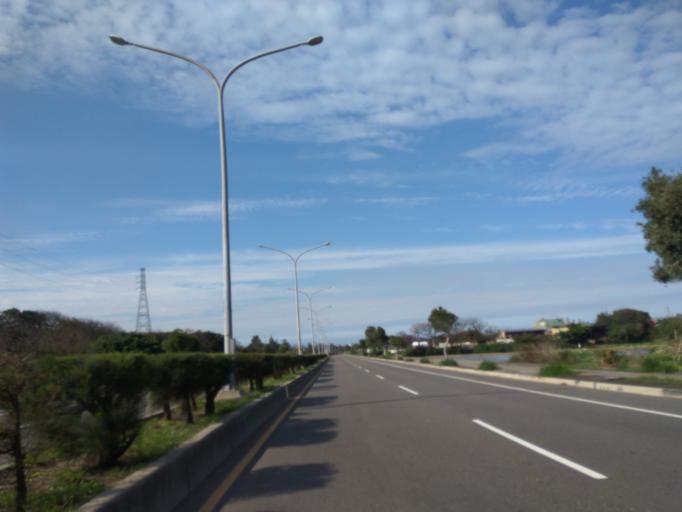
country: TW
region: Taiwan
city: Taoyuan City
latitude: 25.0654
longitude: 121.1758
